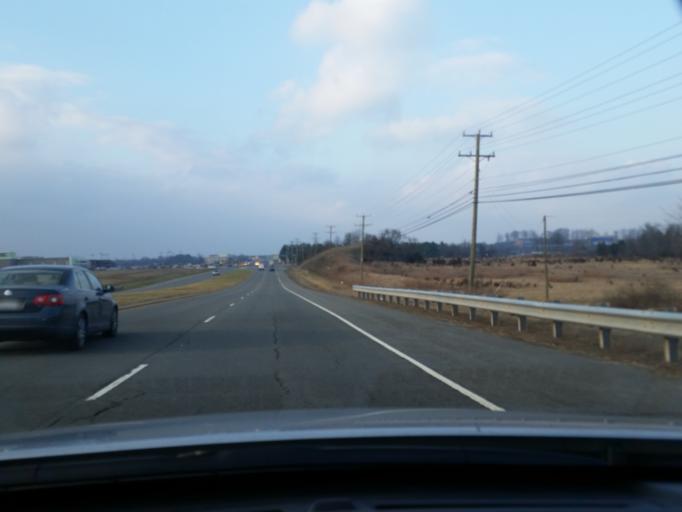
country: US
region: Virginia
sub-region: Loudoun County
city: University Center
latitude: 39.0458
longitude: -77.4503
